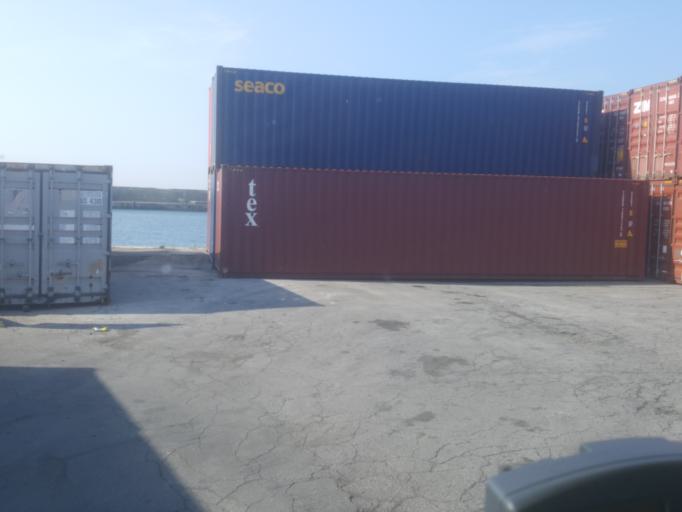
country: IT
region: Liguria
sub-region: Provincia di Genova
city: San Teodoro
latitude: 44.4036
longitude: 8.8905
